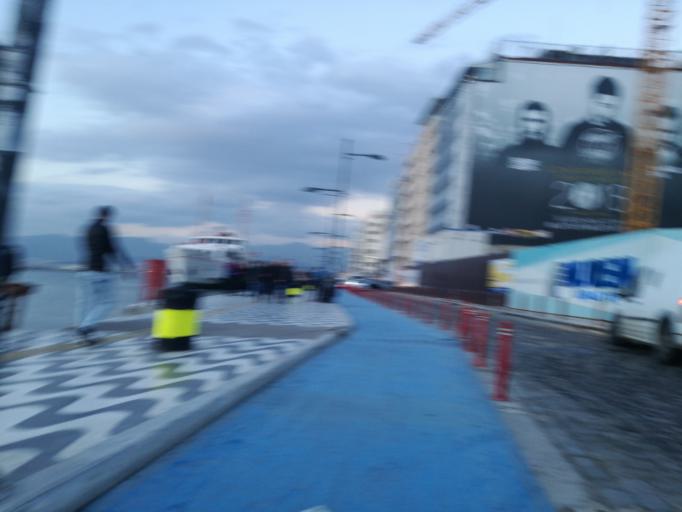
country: TR
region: Izmir
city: Izmir
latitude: 38.4246
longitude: 27.1315
